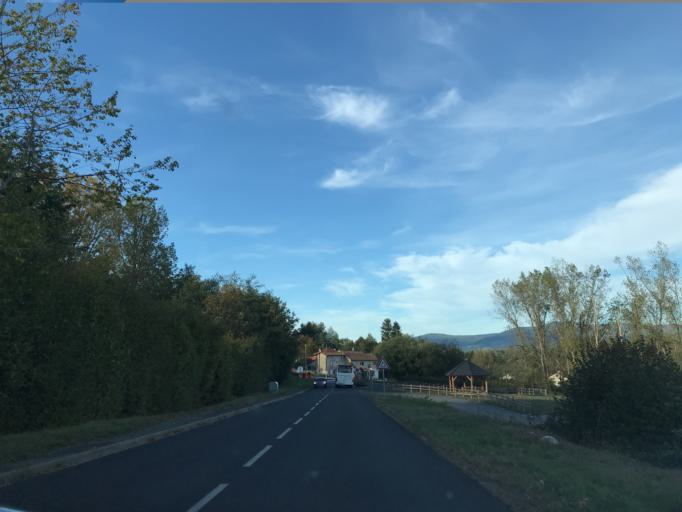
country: FR
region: Auvergne
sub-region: Departement du Puy-de-Dome
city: Celles-sur-Durolle
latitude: 45.8574
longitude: 3.6382
